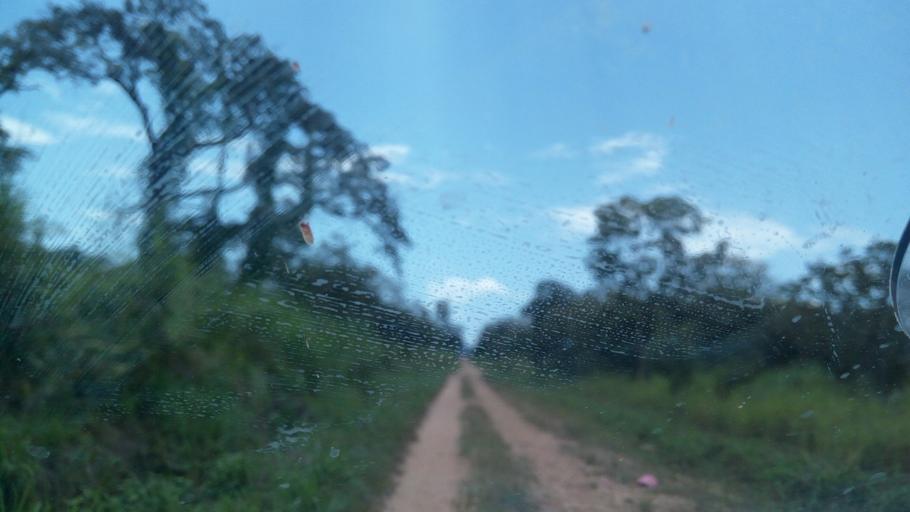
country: TZ
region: Kigoma
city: Kigoma
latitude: -4.8807
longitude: 28.7335
